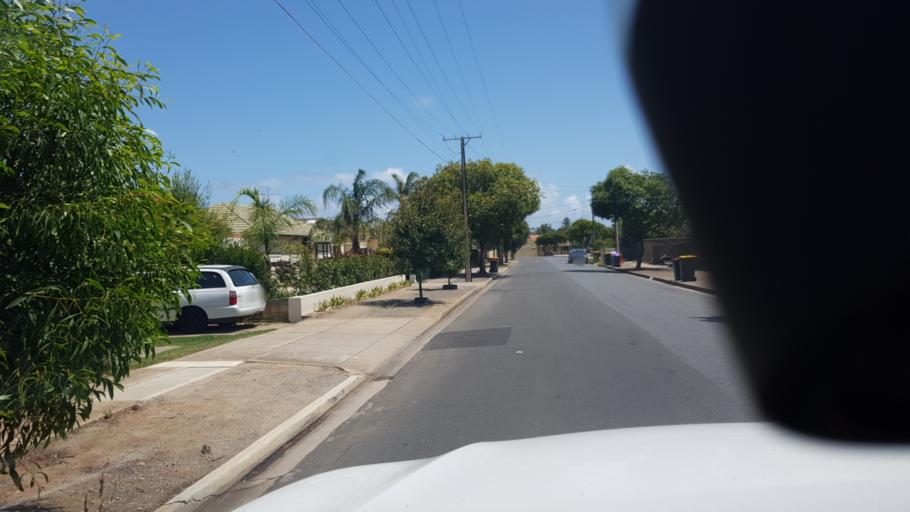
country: AU
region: South Australia
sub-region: Holdfast Bay
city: North Brighton
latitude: -34.9914
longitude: 138.5285
